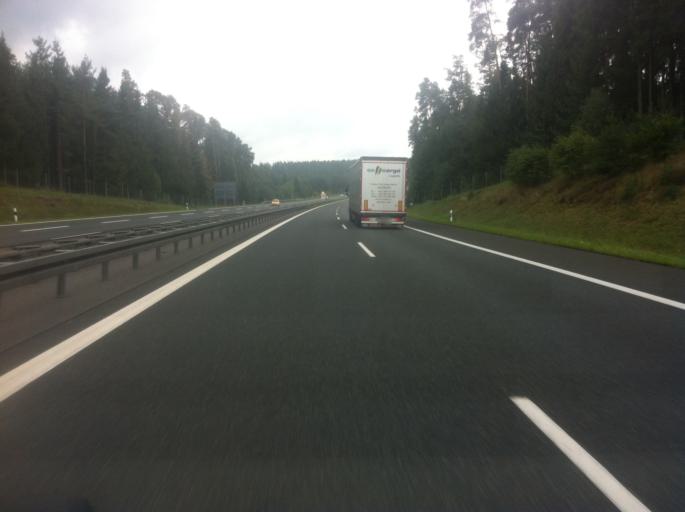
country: DE
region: Bavaria
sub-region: Upper Palatinate
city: Wernberg-Koblitz
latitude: 49.5383
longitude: 12.1923
